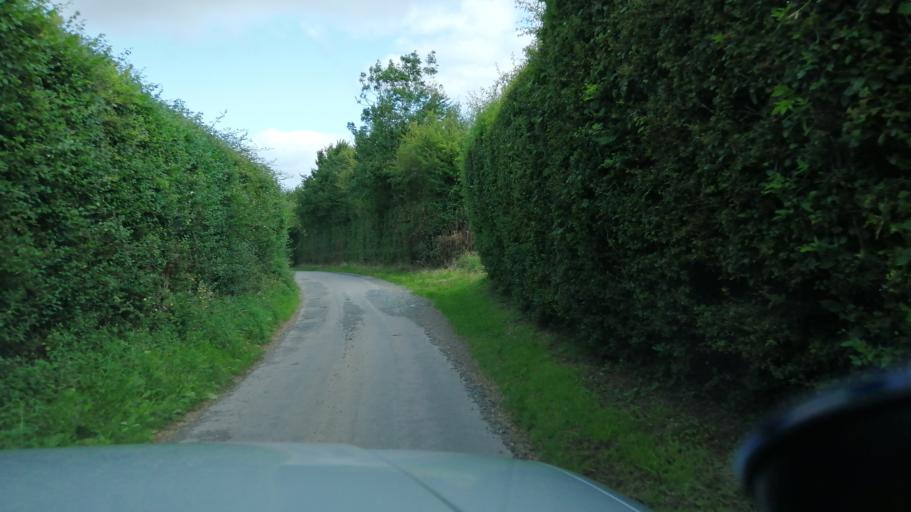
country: GB
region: England
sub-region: Herefordshire
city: Thruxton
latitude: 52.0203
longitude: -2.8015
